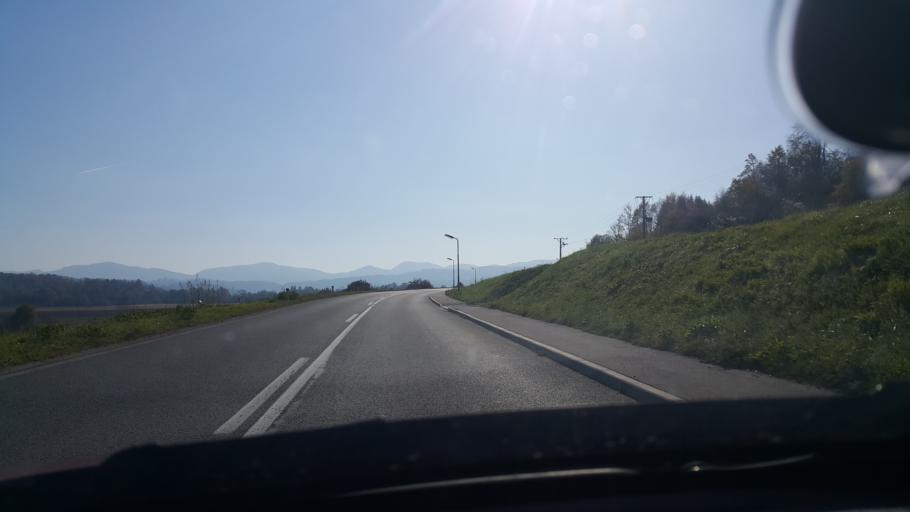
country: SI
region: Podcetrtek
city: Podcetrtek
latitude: 46.1258
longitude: 15.5999
